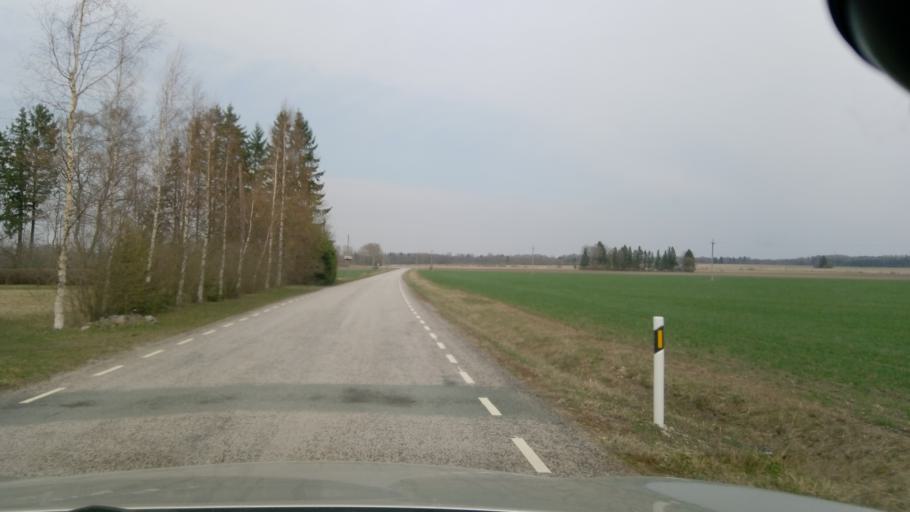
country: EE
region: Jaervamaa
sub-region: Tueri vald
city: Tueri
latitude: 58.7887
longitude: 25.4752
